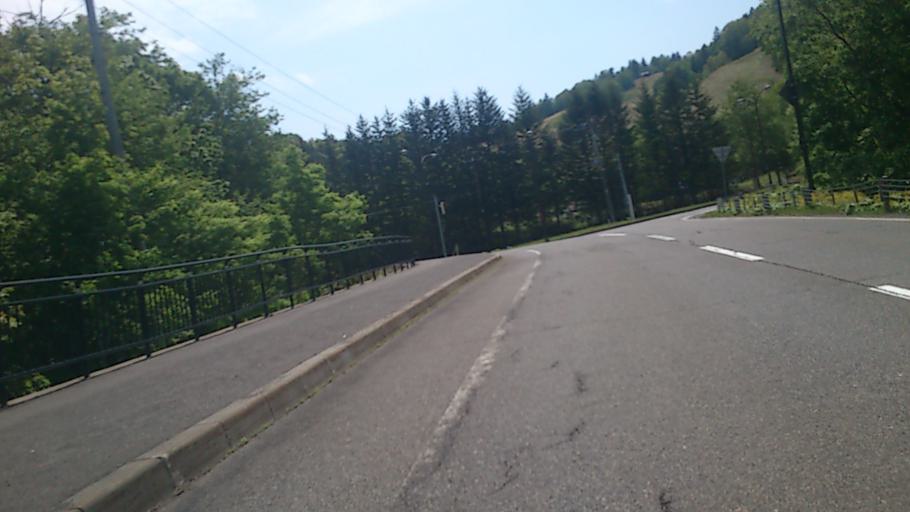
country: JP
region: Hokkaido
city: Otofuke
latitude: 43.3653
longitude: 143.1854
